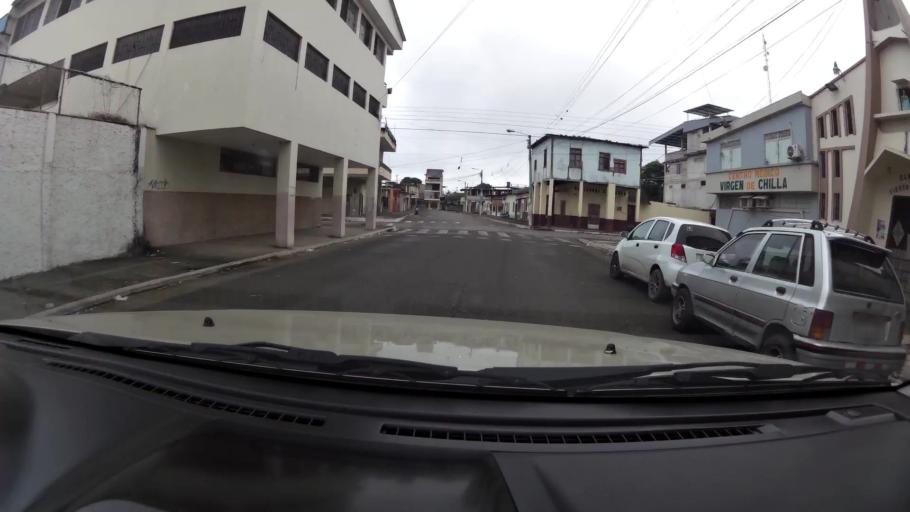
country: EC
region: El Oro
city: Pasaje
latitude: -3.3232
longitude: -79.8042
